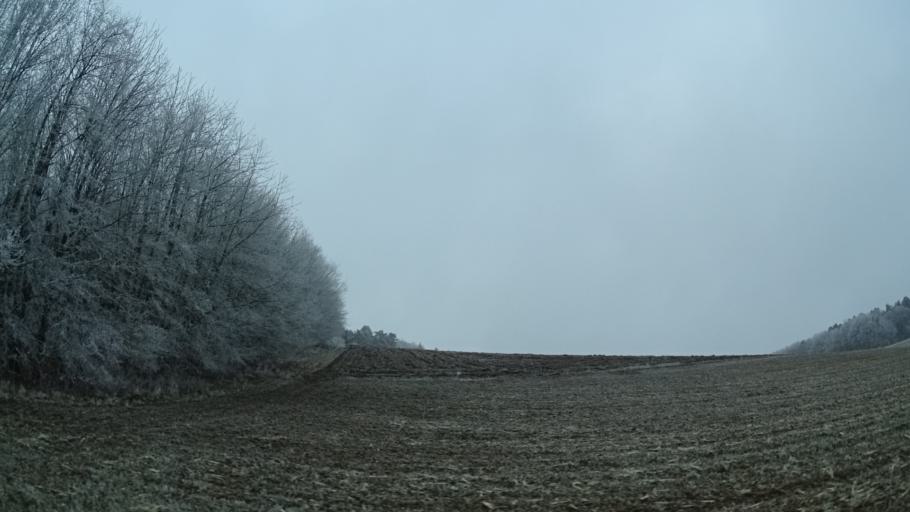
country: DE
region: Baden-Wuerttemberg
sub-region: Regierungsbezirk Stuttgart
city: Boxberg
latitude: 49.5122
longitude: 9.6323
